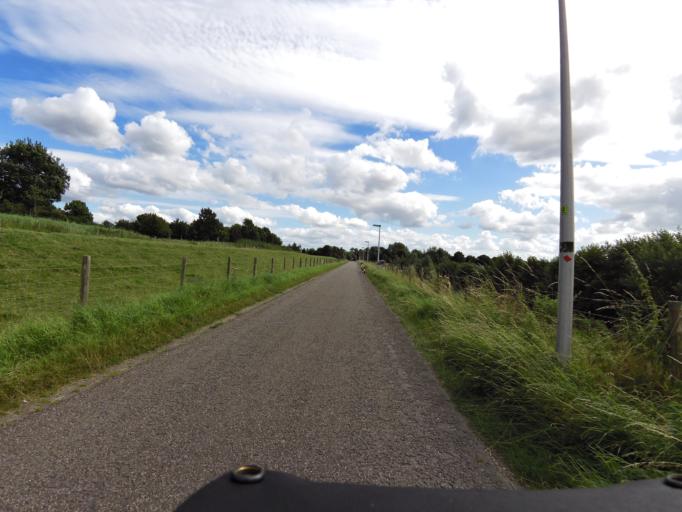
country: NL
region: South Holland
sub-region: Gemeente Spijkenisse
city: Spijkenisse
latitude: 51.8419
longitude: 4.3605
